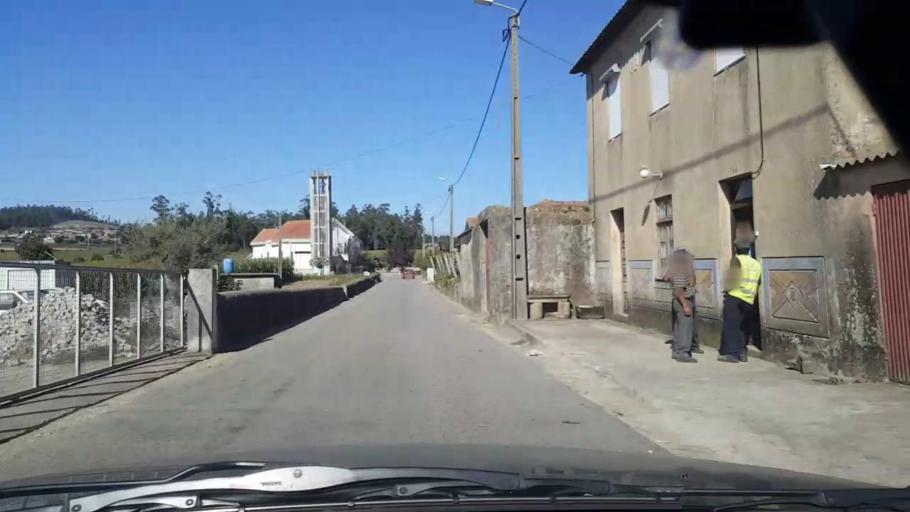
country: PT
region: Braga
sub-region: Vila Nova de Famalicao
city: Ribeirao
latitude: 41.3726
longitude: -8.6440
